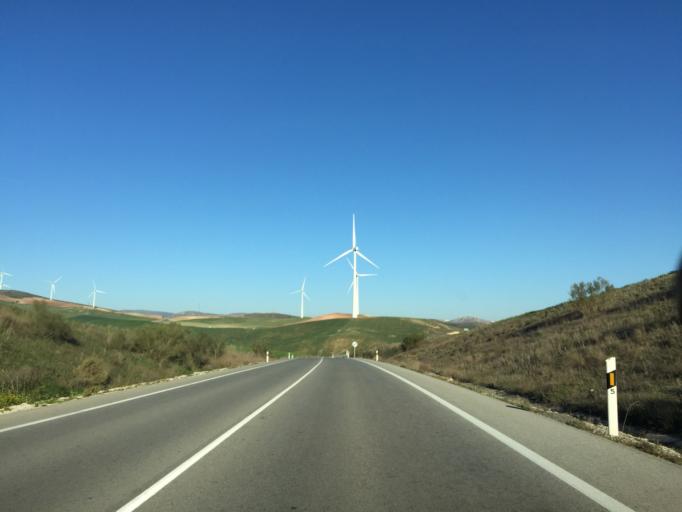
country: ES
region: Andalusia
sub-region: Provincia de Malaga
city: Ardales
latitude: 36.9308
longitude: -4.8567
